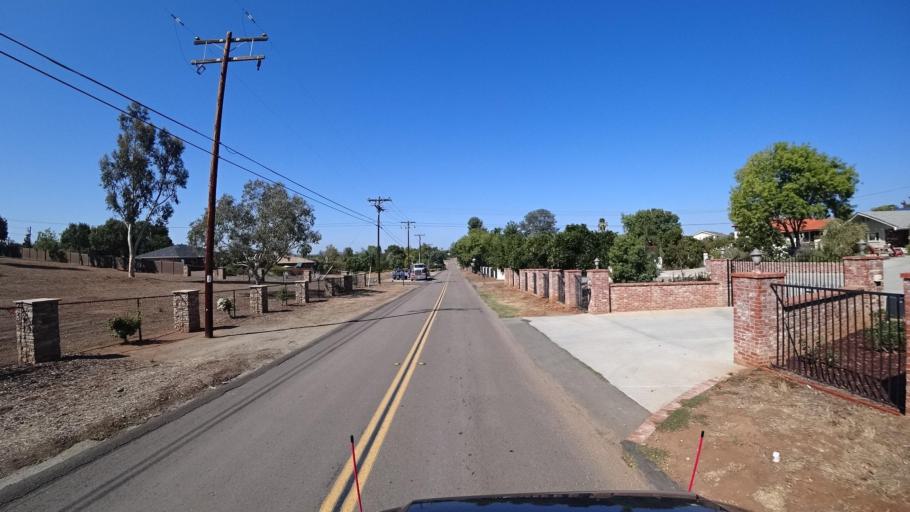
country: US
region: California
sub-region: San Diego County
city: Granite Hills
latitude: 32.7914
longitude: -116.8991
